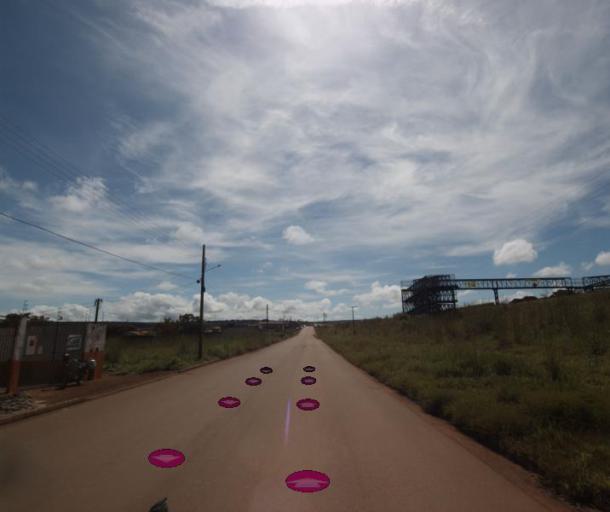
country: BR
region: Federal District
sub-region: Brasilia
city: Brasilia
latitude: -15.7535
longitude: -48.3279
